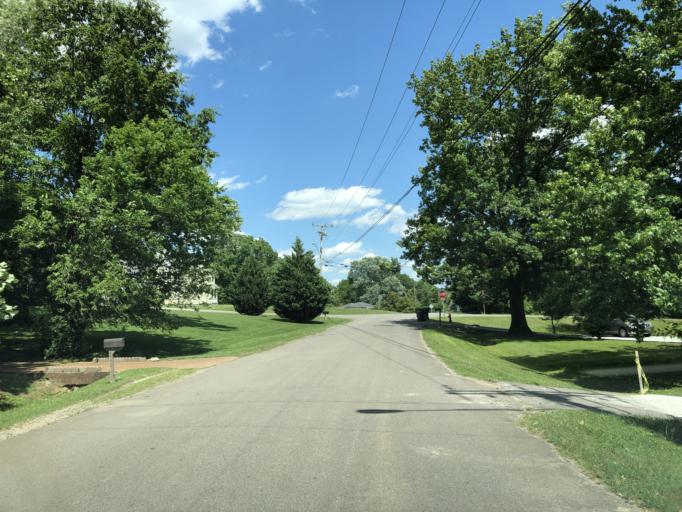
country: US
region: Tennessee
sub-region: Davidson County
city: Nashville
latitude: 36.1758
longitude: -86.7201
